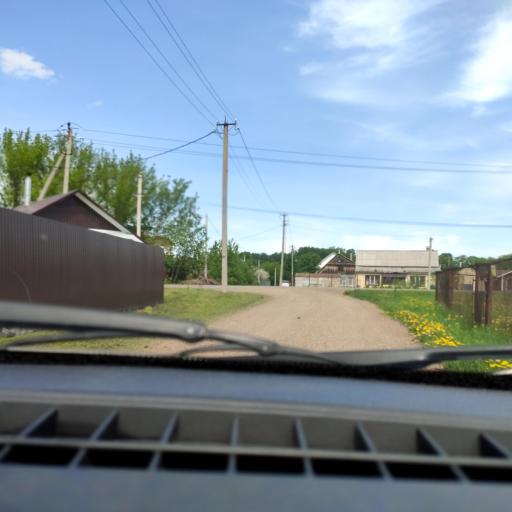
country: RU
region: Bashkortostan
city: Ufa
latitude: 54.5427
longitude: 55.9352
